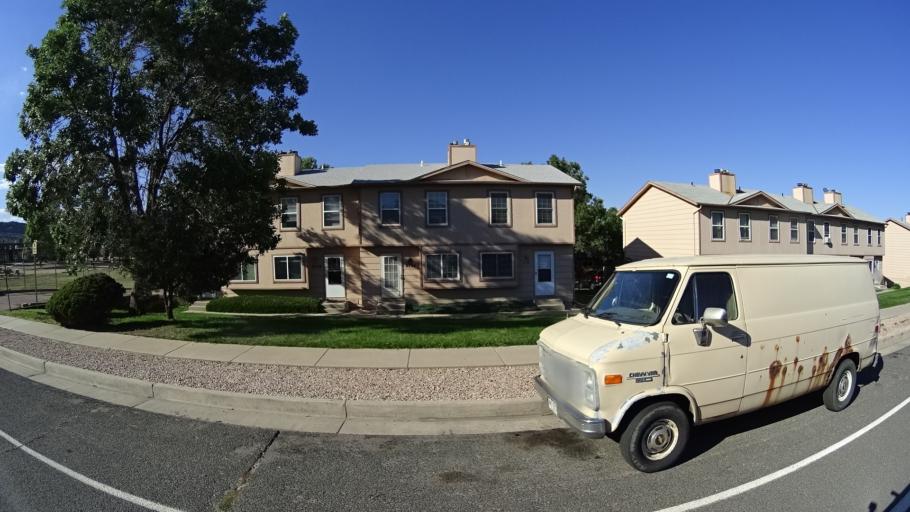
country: US
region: Colorado
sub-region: El Paso County
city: Colorado Springs
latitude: 38.8373
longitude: -104.8614
